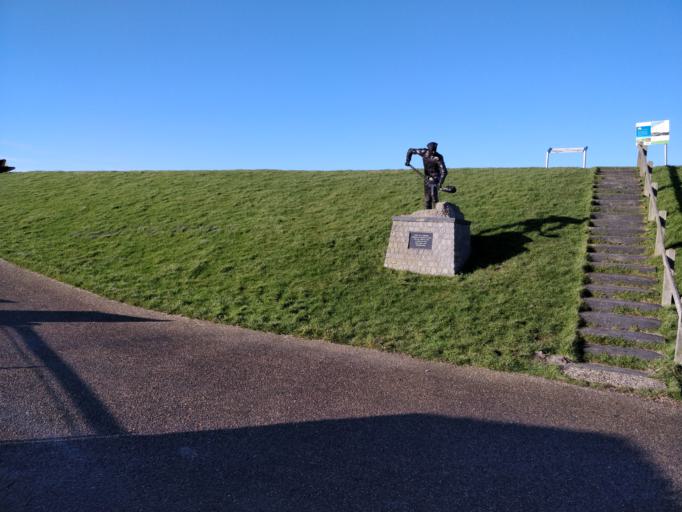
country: NL
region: Friesland
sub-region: Gemeente Het Bildt
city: Sint Jacobiparochie
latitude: 53.3094
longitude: 5.6270
